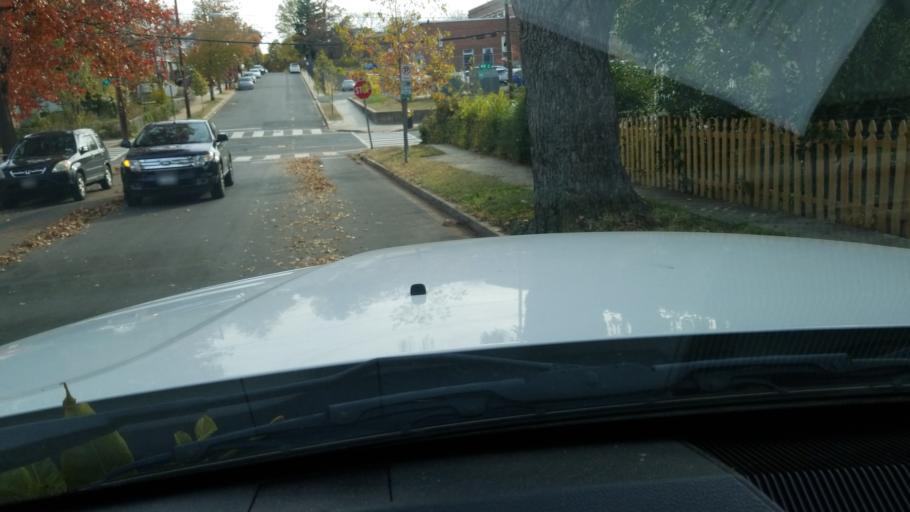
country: US
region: Maryland
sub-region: Prince George's County
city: Fairmount Heights
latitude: 38.8942
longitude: -76.9397
